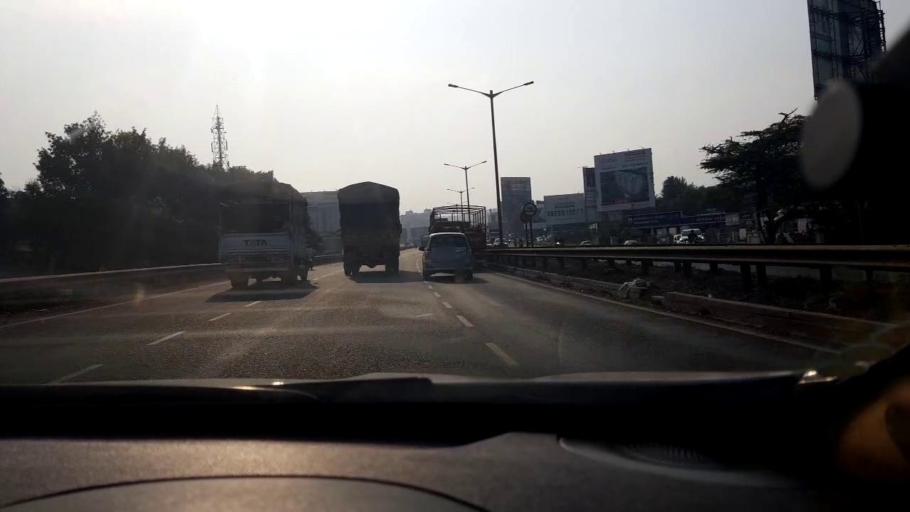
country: IN
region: Maharashtra
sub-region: Pune Division
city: Shivaji Nagar
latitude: 18.5276
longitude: 73.7771
